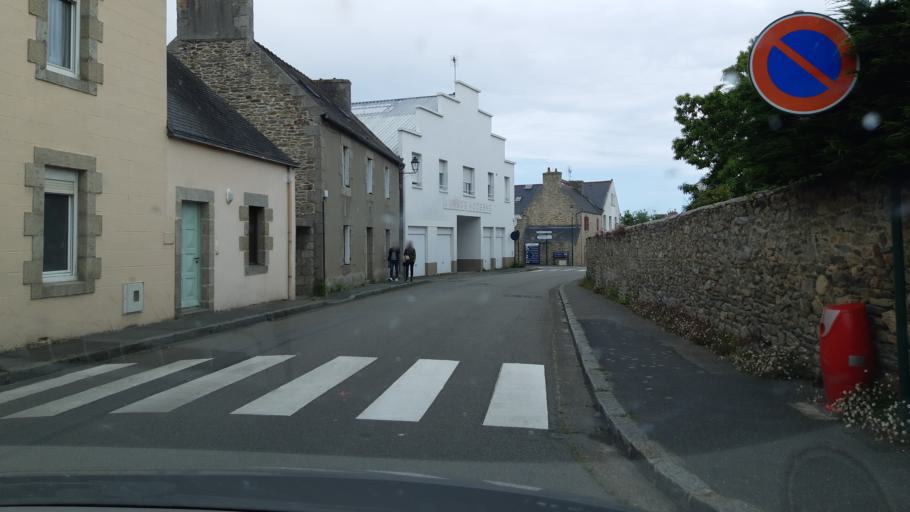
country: FR
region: Brittany
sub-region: Departement du Finistere
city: Roscoff
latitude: 48.7224
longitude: -3.9869
